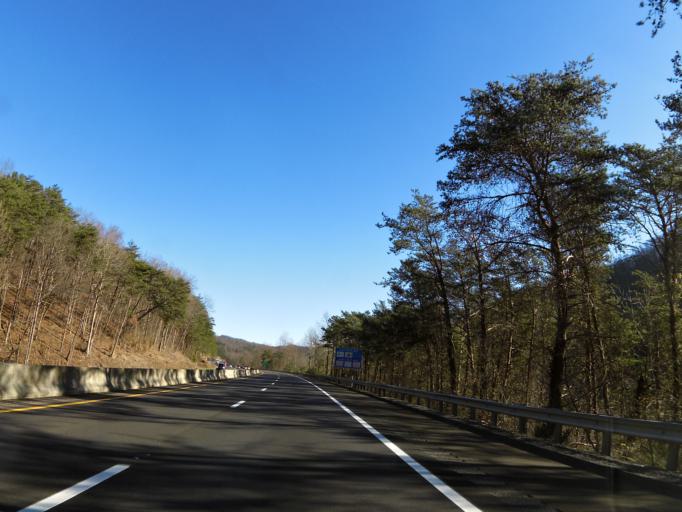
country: US
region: Tennessee
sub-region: Cocke County
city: Newport
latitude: 35.8144
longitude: -83.1653
